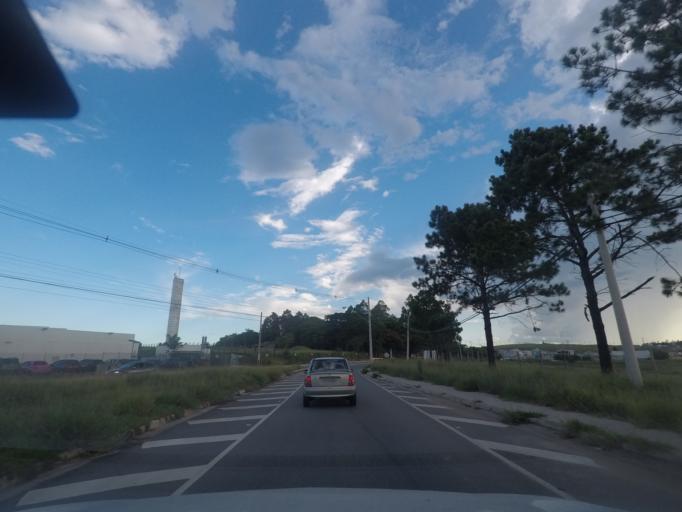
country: BR
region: Sao Paulo
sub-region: Cacapava
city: Cacapava
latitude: -23.1225
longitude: -45.7131
